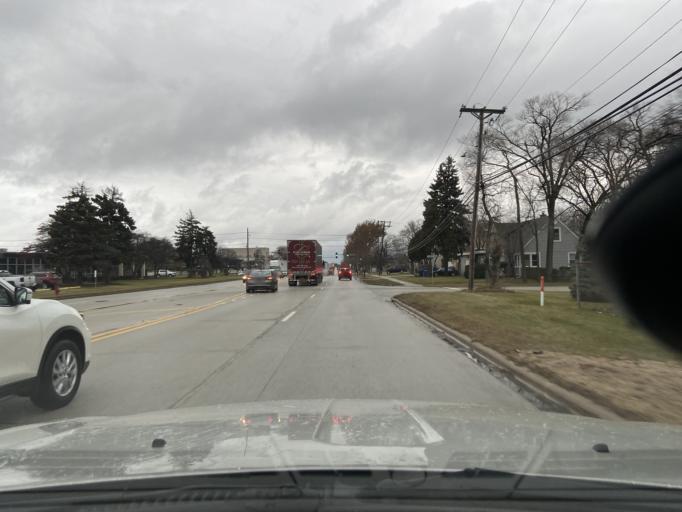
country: US
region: Illinois
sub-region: Cook County
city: Rosemont
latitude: 42.0147
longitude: -87.9089
